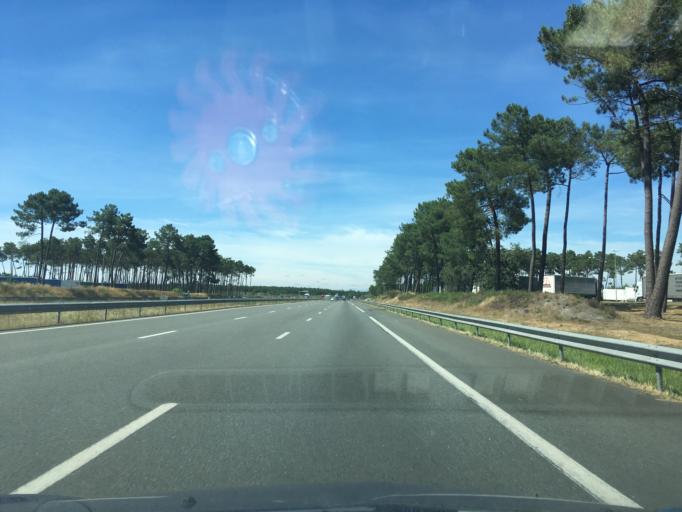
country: FR
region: Aquitaine
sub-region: Departement de la Gironde
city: Salles
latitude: 44.5006
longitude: -0.8407
